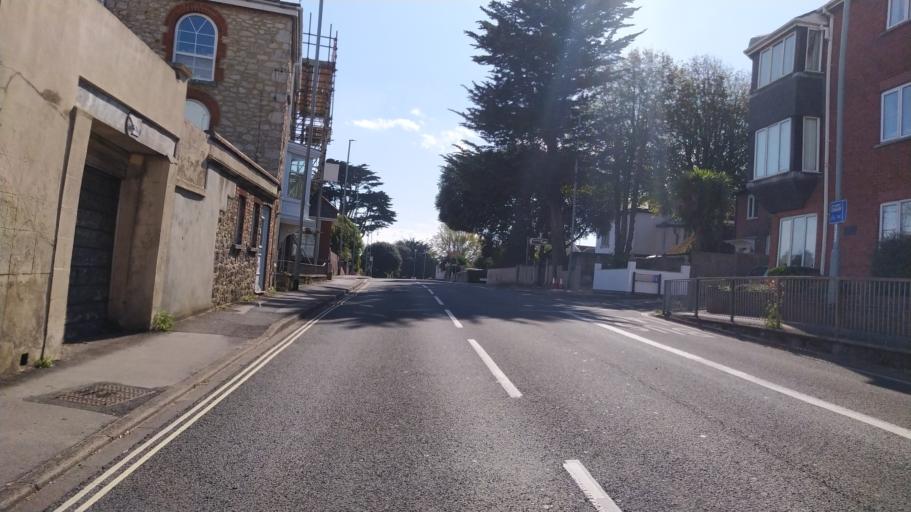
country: GB
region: England
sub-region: Dorset
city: Weymouth
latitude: 50.6022
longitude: -2.4589
